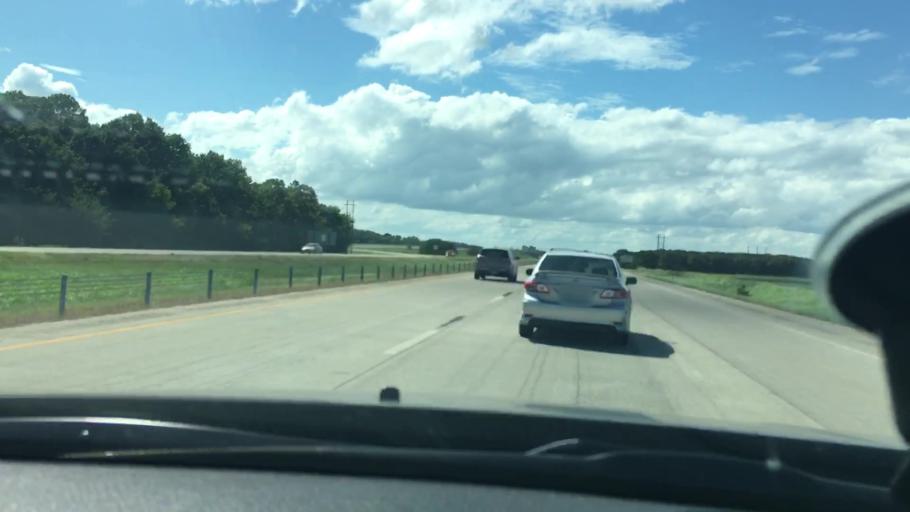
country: US
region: Oklahoma
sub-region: Muskogee County
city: Warner
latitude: 35.4845
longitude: -95.1566
